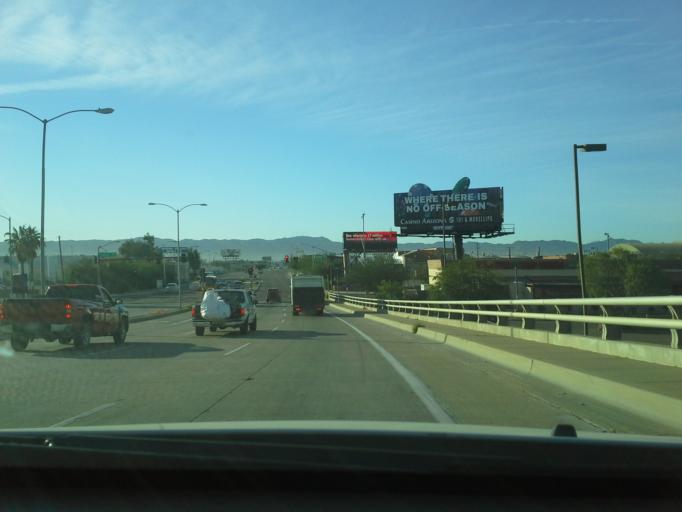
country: US
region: Arizona
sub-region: Maricopa County
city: Phoenix
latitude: 33.4433
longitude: -112.0655
